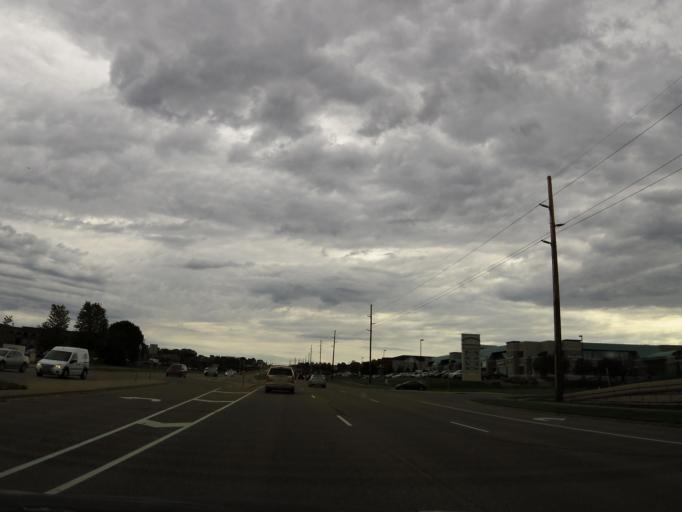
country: US
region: Minnesota
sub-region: Scott County
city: Savage
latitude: 44.7462
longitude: -93.3181
